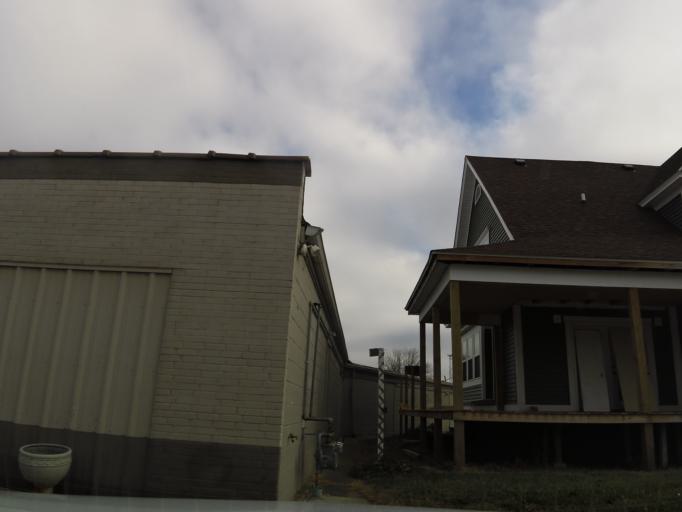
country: US
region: Indiana
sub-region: Bartholomew County
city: Columbus
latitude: 39.1969
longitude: -85.9032
